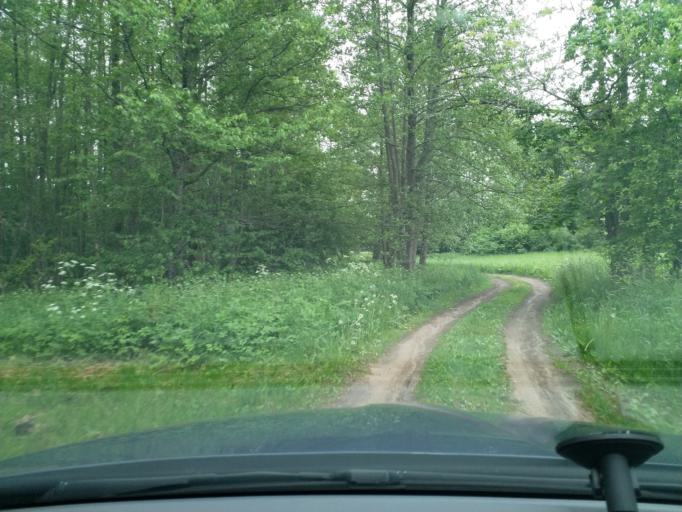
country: LV
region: Kuldigas Rajons
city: Kuldiga
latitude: 56.8757
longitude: 21.8244
